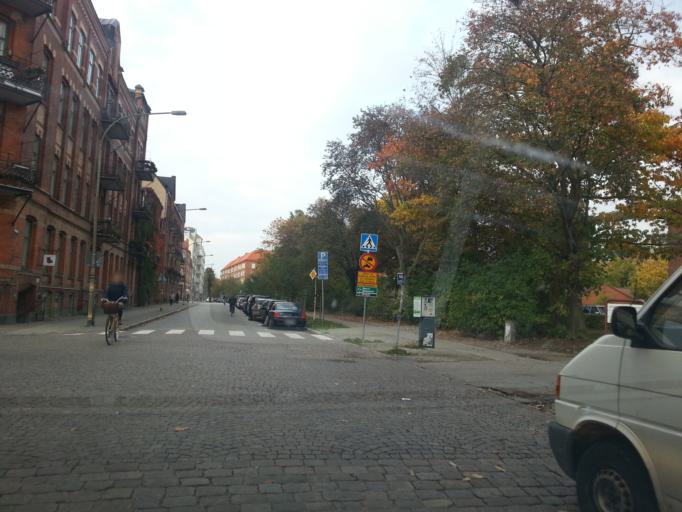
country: SE
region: Skane
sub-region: Lunds Kommun
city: Lund
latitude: 55.7085
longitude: 13.1892
